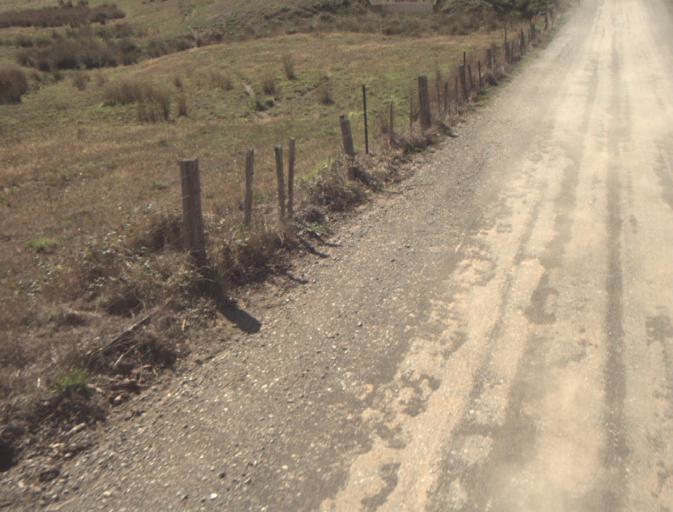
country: AU
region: Tasmania
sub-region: Launceston
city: Mayfield
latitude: -41.2284
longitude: 147.2360
